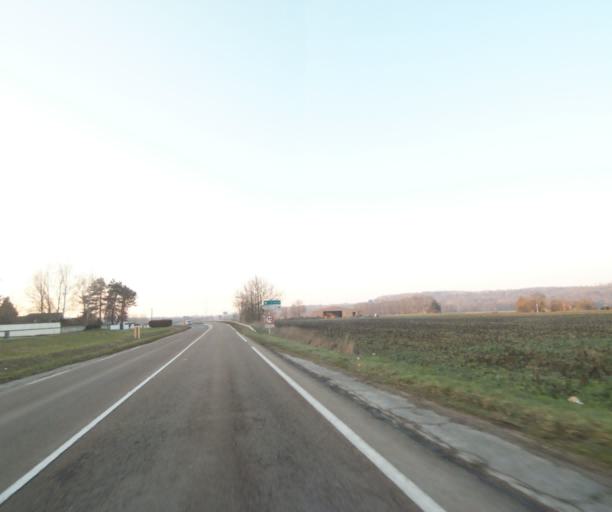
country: FR
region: Champagne-Ardenne
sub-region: Departement de la Haute-Marne
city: Bienville
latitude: 48.6039
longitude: 5.0298
